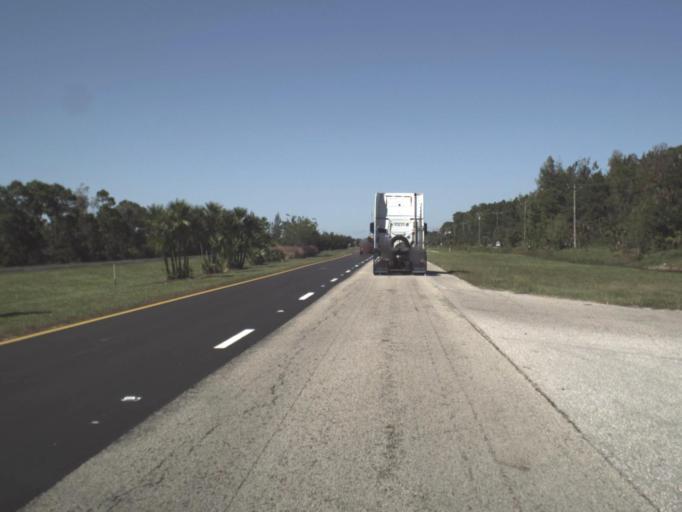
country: US
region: Florida
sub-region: Lee County
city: Suncoast Estates
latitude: 26.7576
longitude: -81.9243
